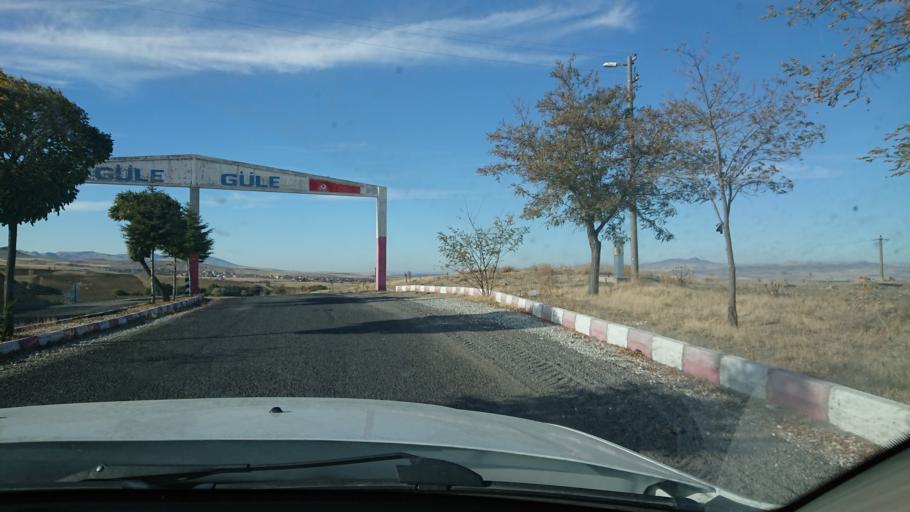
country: TR
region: Aksaray
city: Sariyahsi
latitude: 38.9676
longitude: 33.8722
